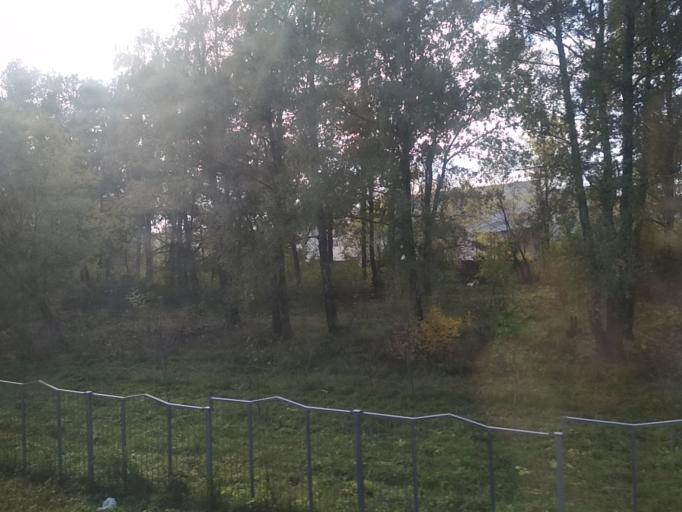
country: BY
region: Minsk
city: Syenitsa
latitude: 53.8390
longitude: 27.5601
